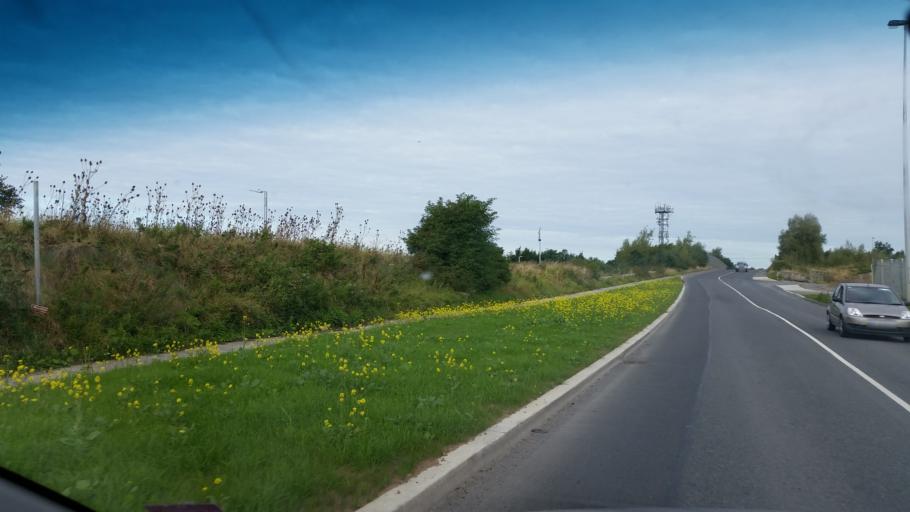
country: IE
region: Leinster
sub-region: Dublin City
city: Finglas
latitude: 53.3957
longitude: -6.3290
